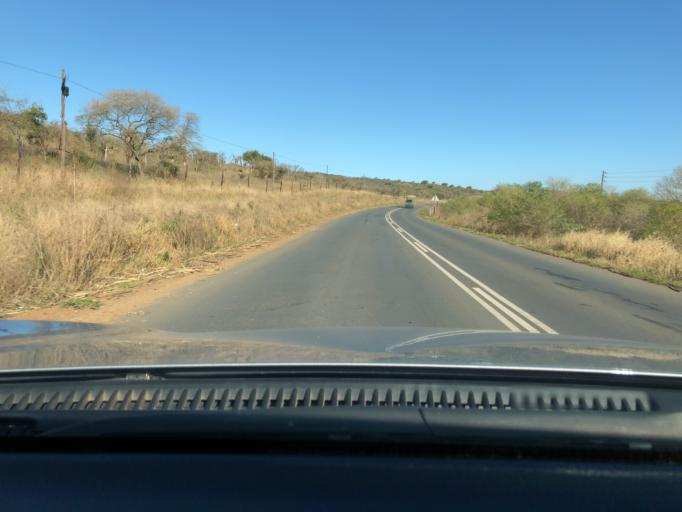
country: ZA
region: KwaZulu-Natal
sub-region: uMgungundlovu District Municipality
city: Camperdown
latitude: -29.8082
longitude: 30.5202
